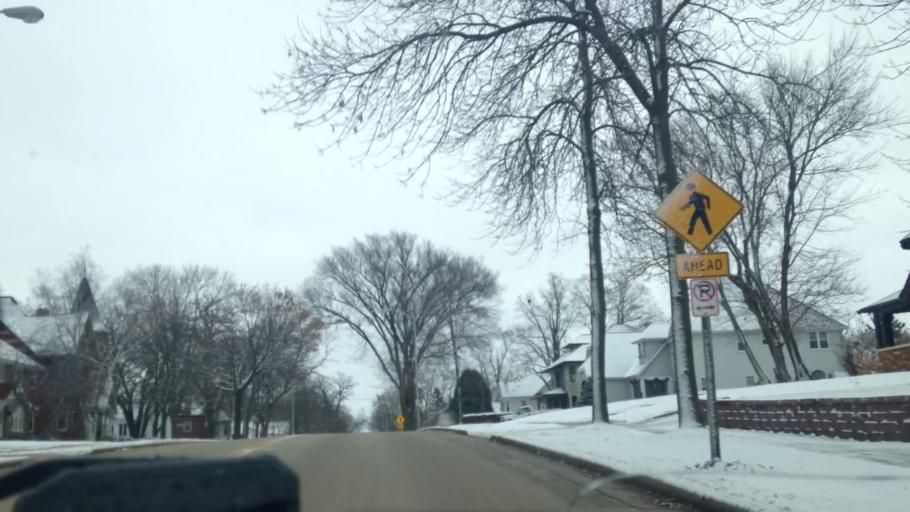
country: US
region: Wisconsin
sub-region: Dodge County
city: Beaver Dam
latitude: 43.4563
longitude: -88.8331
